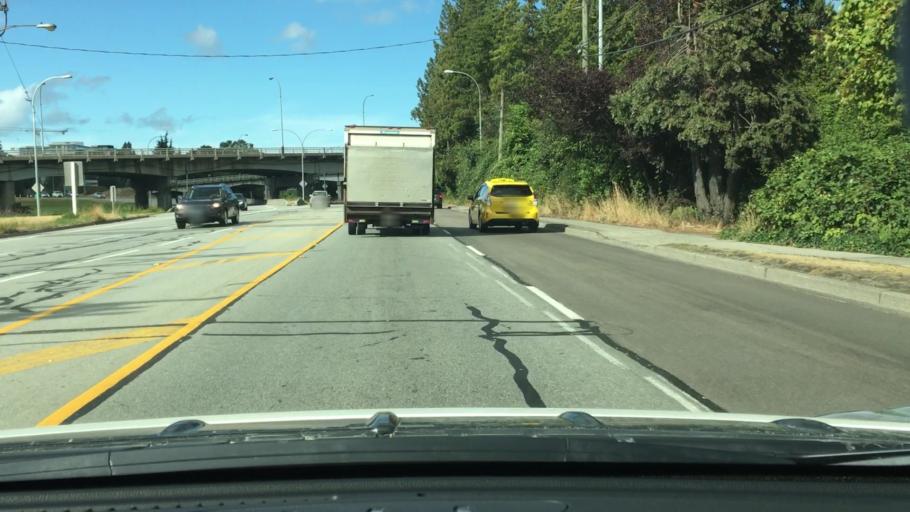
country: CA
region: British Columbia
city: Richmond
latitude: 49.1920
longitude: -123.1165
